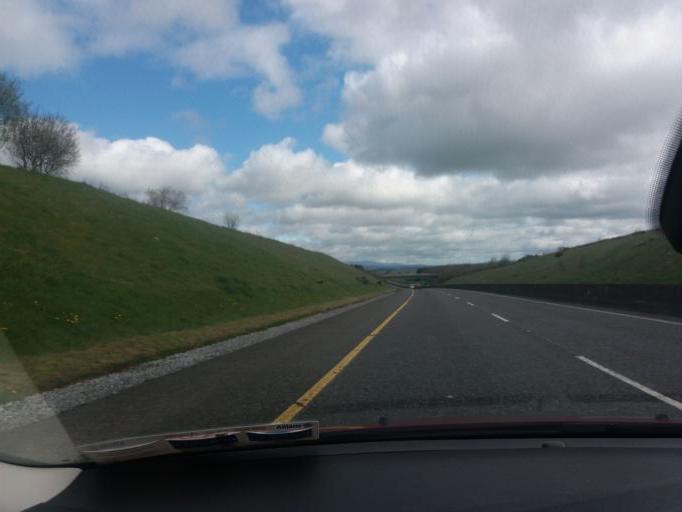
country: IE
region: Munster
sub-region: County Cork
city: Watergrasshill
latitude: 52.0350
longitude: -8.3189
